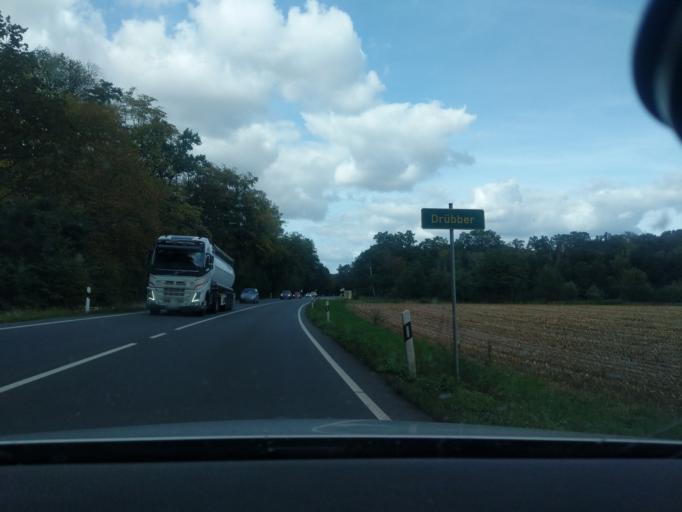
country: DE
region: Lower Saxony
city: Eystrup
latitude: 52.8153
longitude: 9.1991
